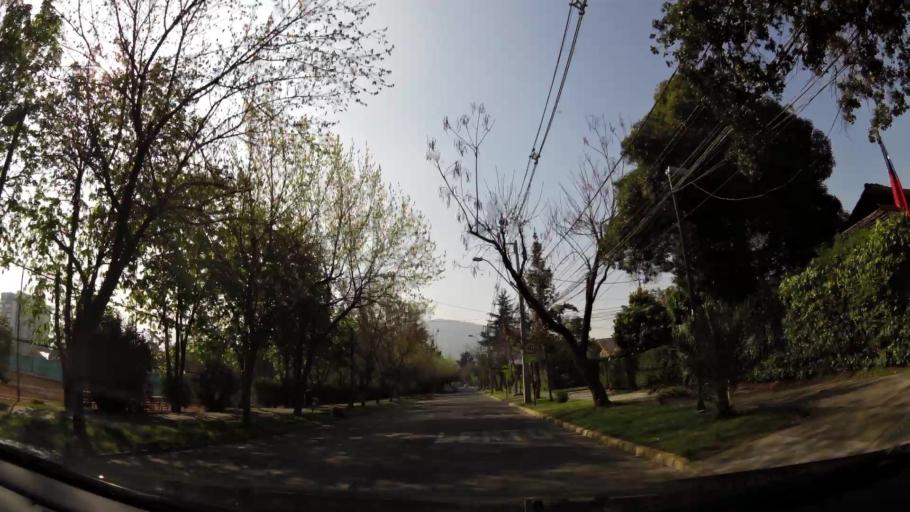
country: CL
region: Santiago Metropolitan
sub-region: Provincia de Santiago
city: Villa Presidente Frei, Nunoa, Santiago, Chile
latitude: -33.3873
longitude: -70.5560
